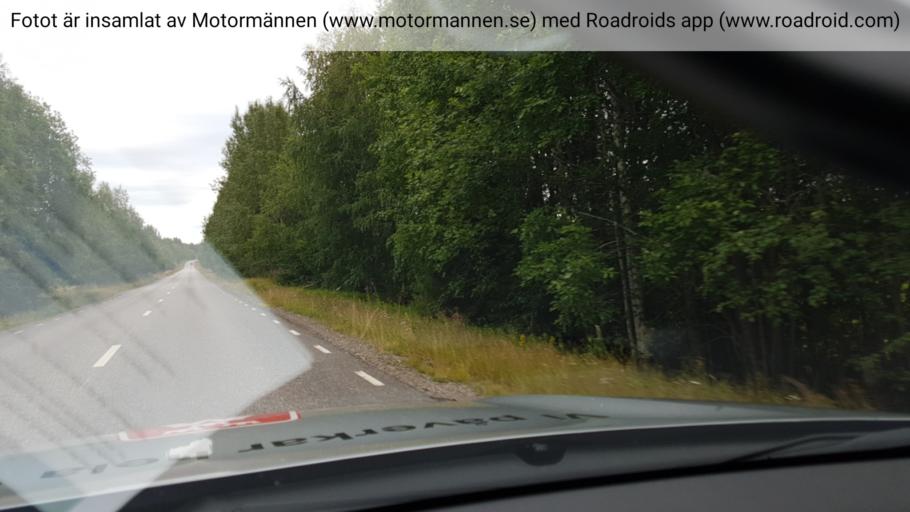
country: SE
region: Norrbotten
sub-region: Overkalix Kommun
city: OEverkalix
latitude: 66.5017
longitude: 22.7678
